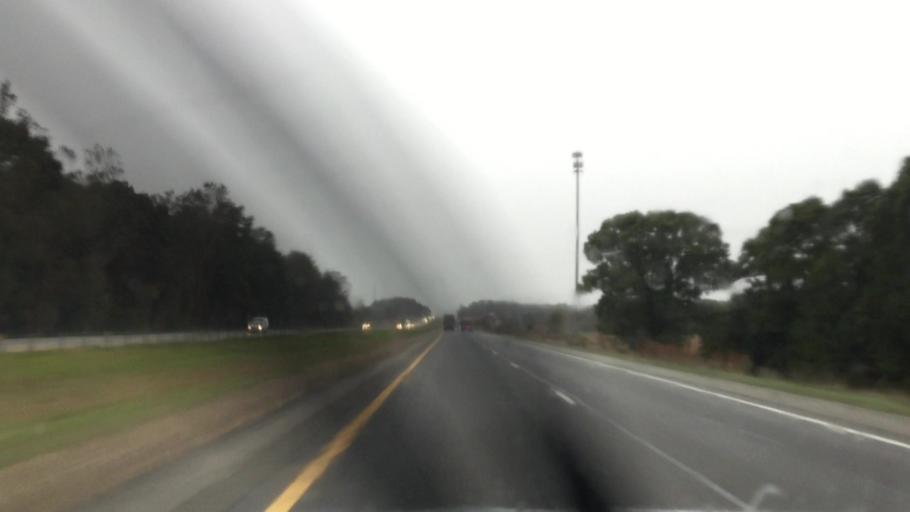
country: US
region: Michigan
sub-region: Van Buren County
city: Mattawan
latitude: 42.2233
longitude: -85.7493
